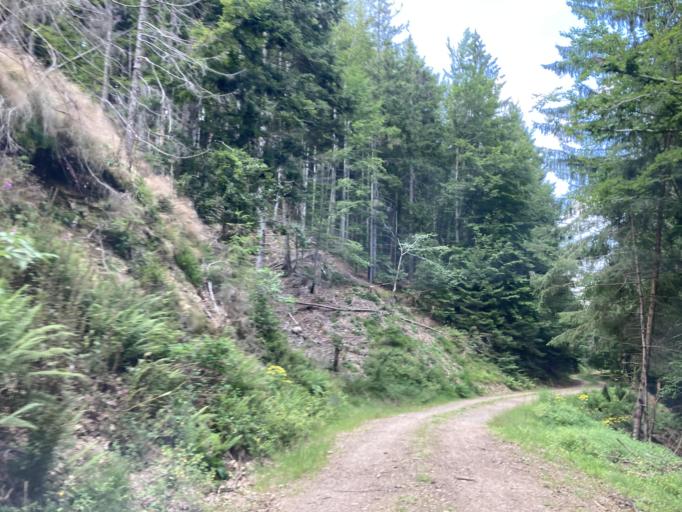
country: DE
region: Baden-Wuerttemberg
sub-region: Freiburg Region
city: Schonach im Schwarzwald
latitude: 48.1574
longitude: 8.1547
